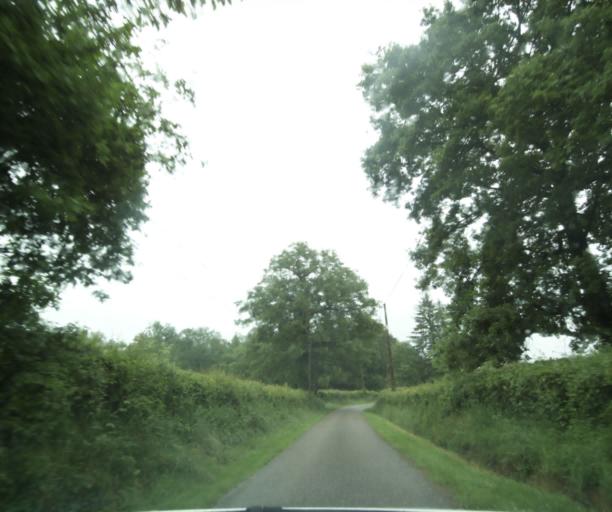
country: FR
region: Bourgogne
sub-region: Departement de Saone-et-Loire
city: Paray-le-Monial
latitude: 46.4125
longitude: 4.1895
